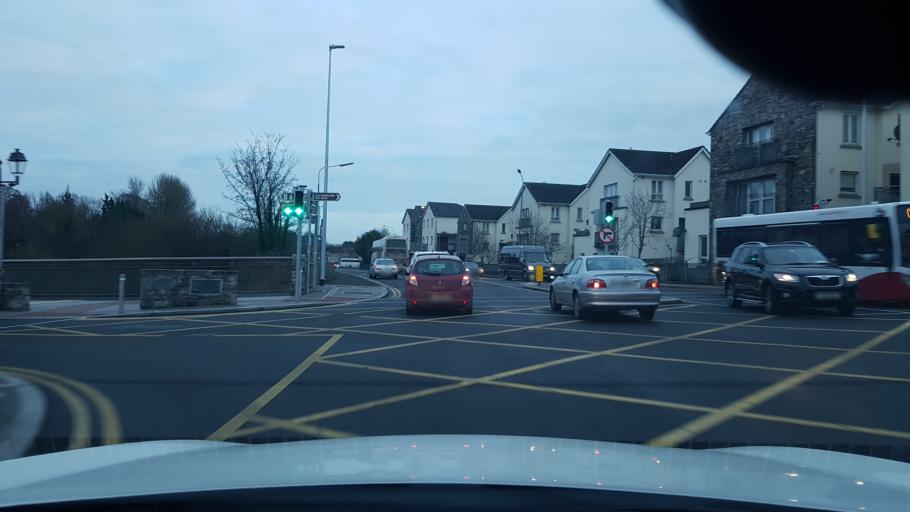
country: IE
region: Leinster
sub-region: An Mhi
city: Navan
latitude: 53.6534
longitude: -6.6824
